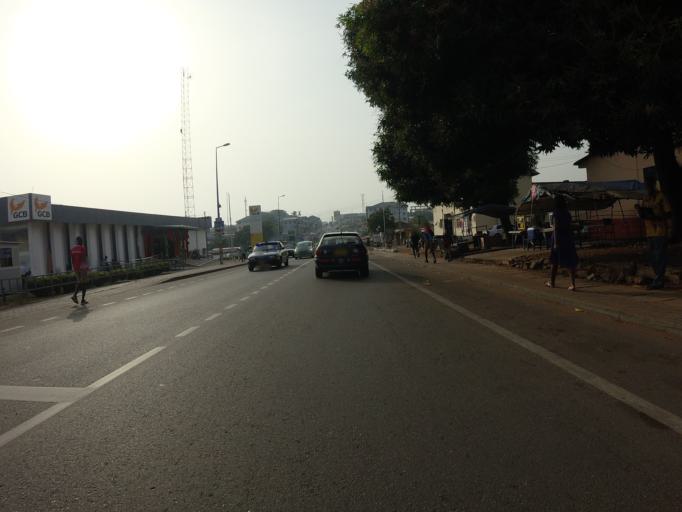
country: GH
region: Volta
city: Ho
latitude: 6.6108
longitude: 0.4707
